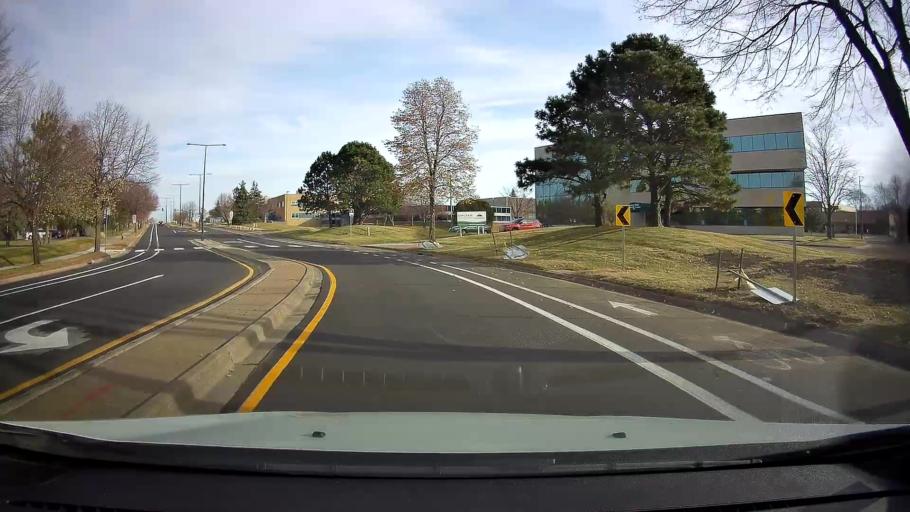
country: US
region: Minnesota
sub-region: Ramsey County
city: Falcon Heights
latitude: 44.9709
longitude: -93.1580
